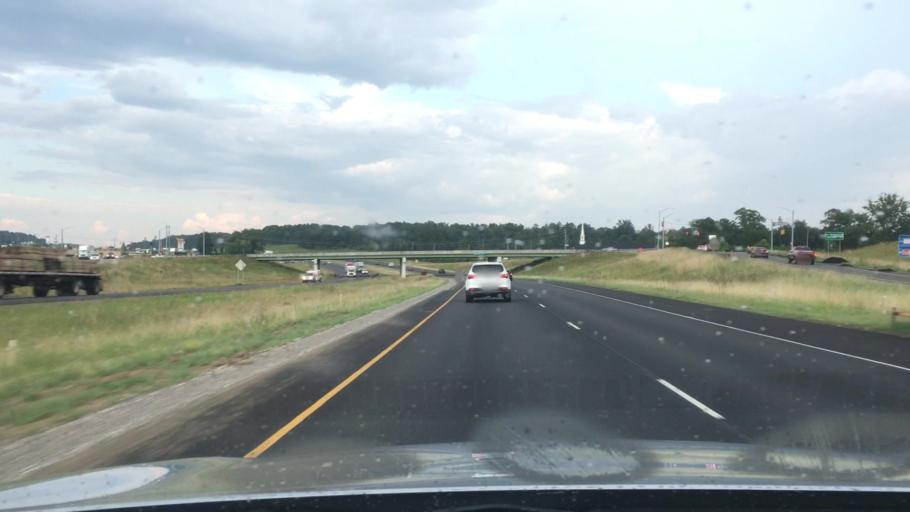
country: US
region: Alabama
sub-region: Jefferson County
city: Bessemer
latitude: 33.3333
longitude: -87.0006
